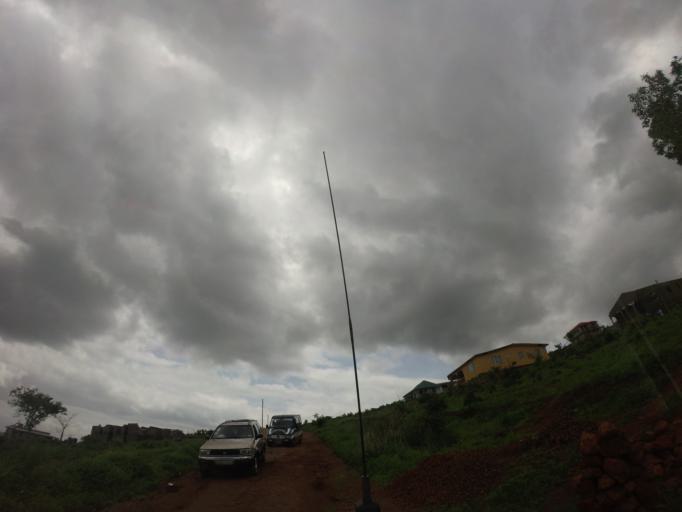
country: SL
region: Western Area
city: Hastings
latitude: 8.3853
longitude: -13.1258
